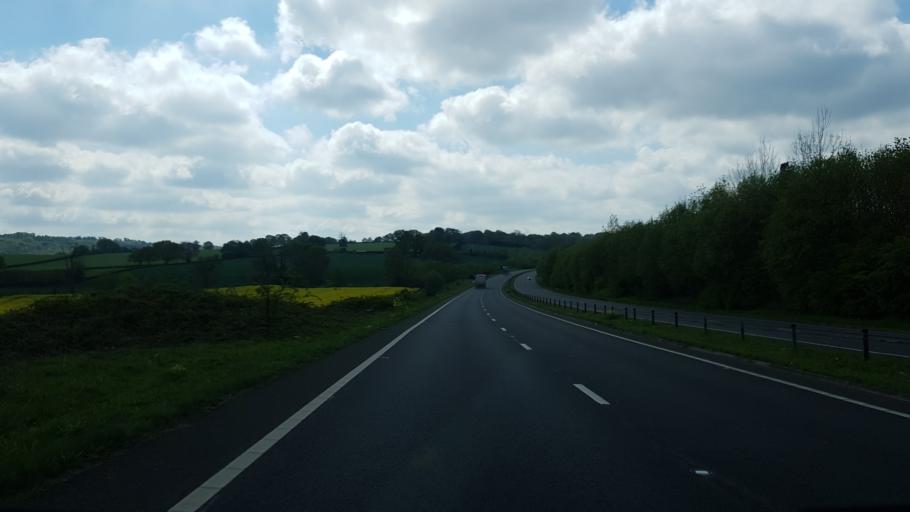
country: GB
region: England
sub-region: East Sussex
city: Wadhurst
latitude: 51.1057
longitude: 0.4045
